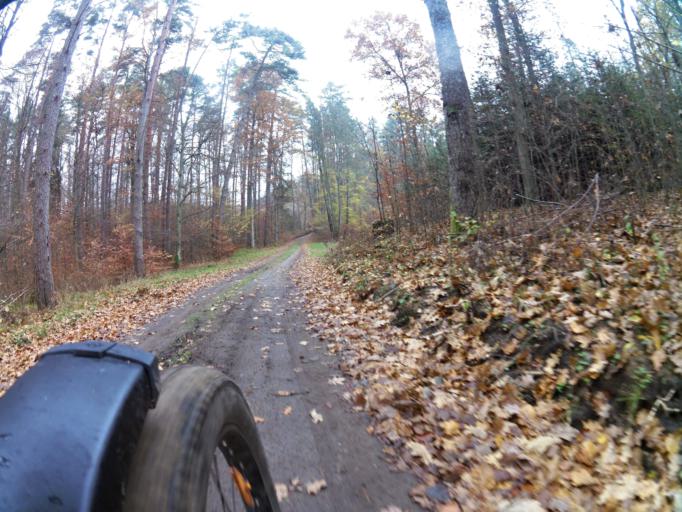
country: PL
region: Pomeranian Voivodeship
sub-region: Powiat wejherowski
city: Orle
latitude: 54.6951
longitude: 18.1562
